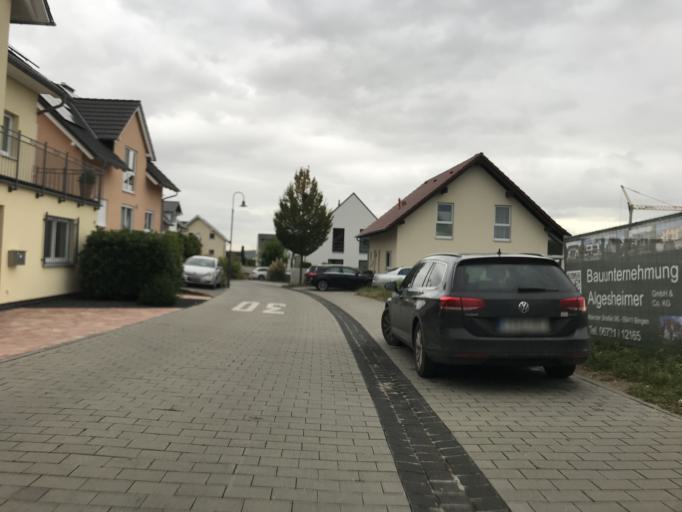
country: DE
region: Rheinland-Pfalz
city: Schwabenheim
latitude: 49.9275
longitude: 8.1007
